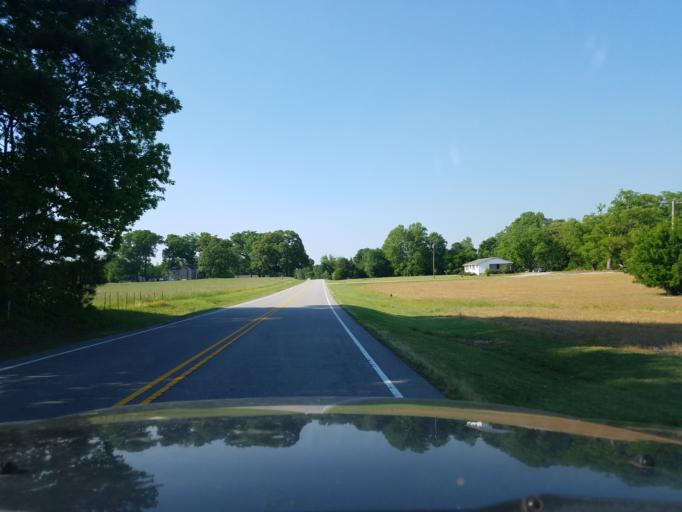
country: US
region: North Carolina
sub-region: Vance County
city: Henderson
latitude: 36.3954
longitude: -78.3684
